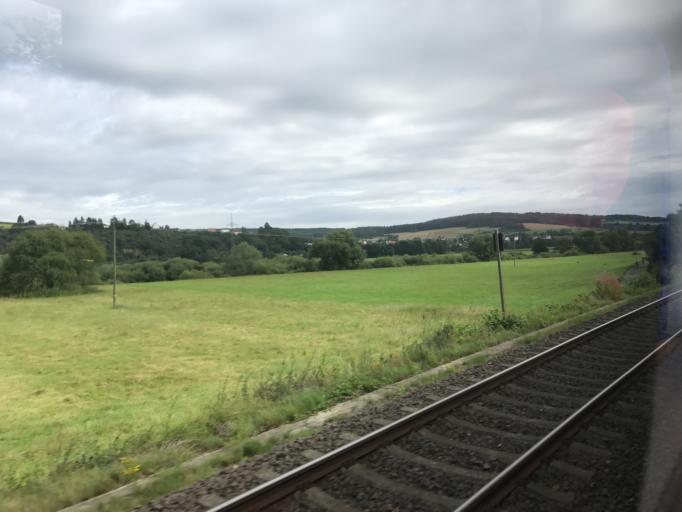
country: DE
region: Hesse
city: Niederbiel
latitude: 50.5461
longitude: 8.3947
